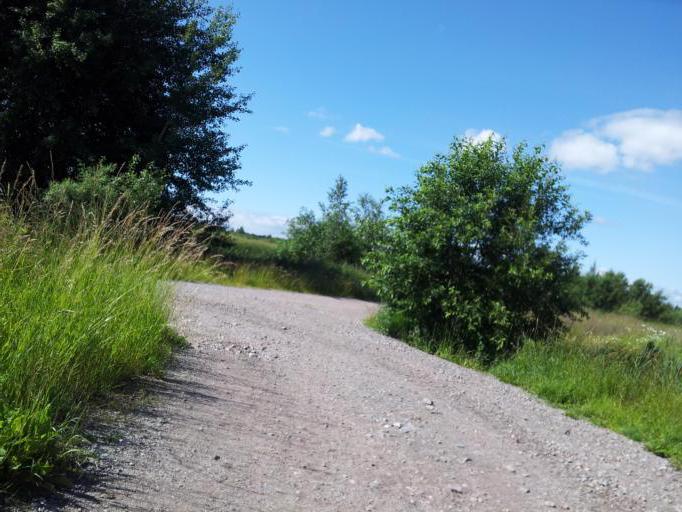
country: SE
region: Uppsala
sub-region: Uppsala Kommun
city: Saevja
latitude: 59.8697
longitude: 17.7113
